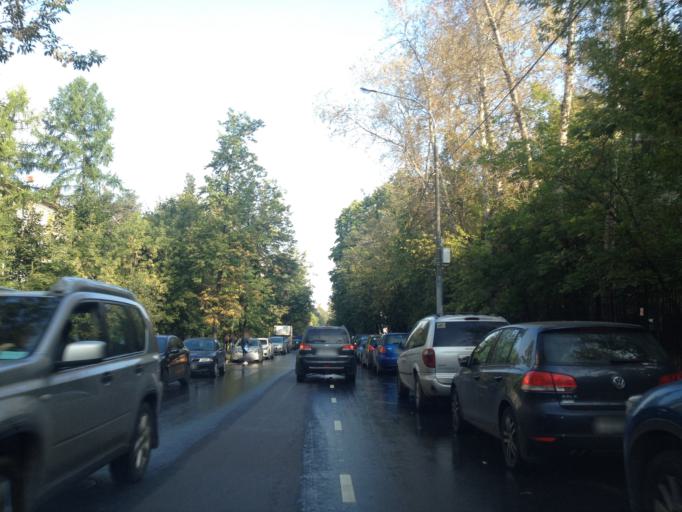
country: RU
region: Moskovskaya
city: Izmaylovo
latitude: 55.7946
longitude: 37.7939
